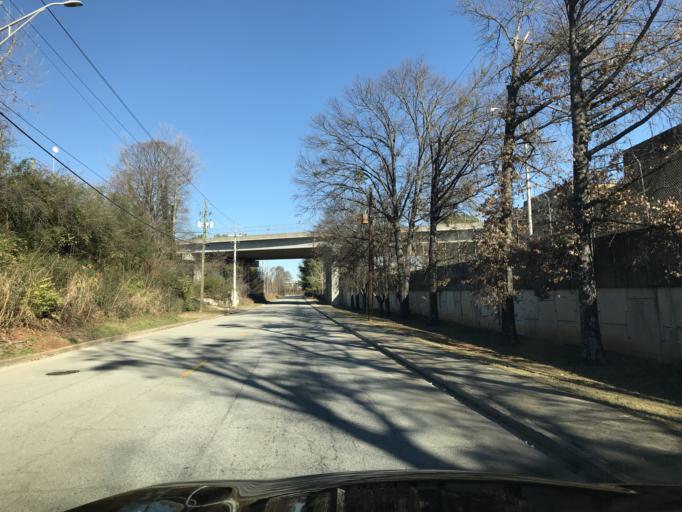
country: US
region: Georgia
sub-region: Fulton County
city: College Park
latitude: 33.6356
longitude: -84.4580
